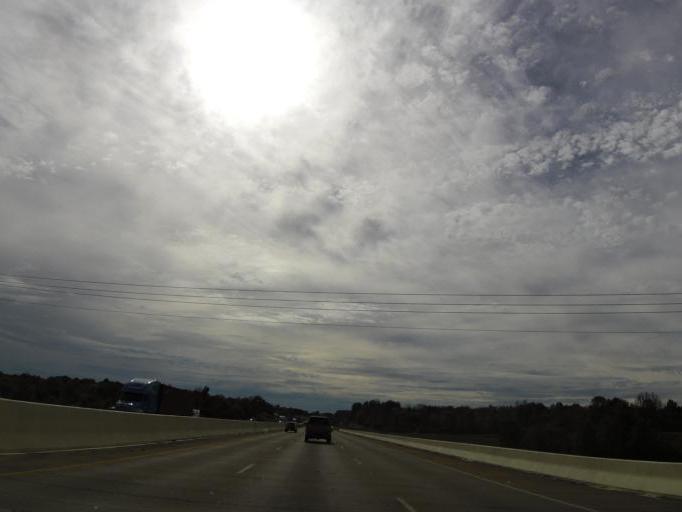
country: US
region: Ohio
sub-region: Summit County
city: Silver Lake
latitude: 41.2032
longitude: -81.4833
